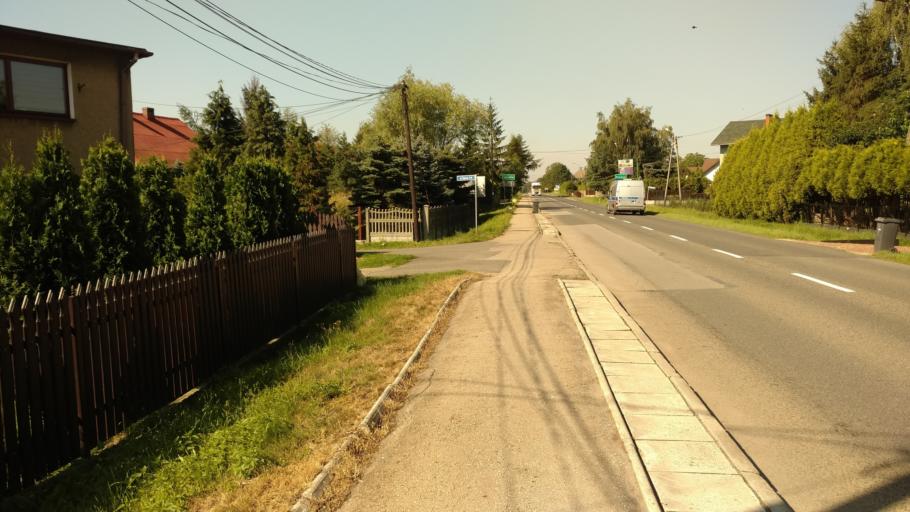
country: PL
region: Silesian Voivodeship
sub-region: Powiat pszczynski
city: Pszczyna
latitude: 49.9944
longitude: 18.9668
